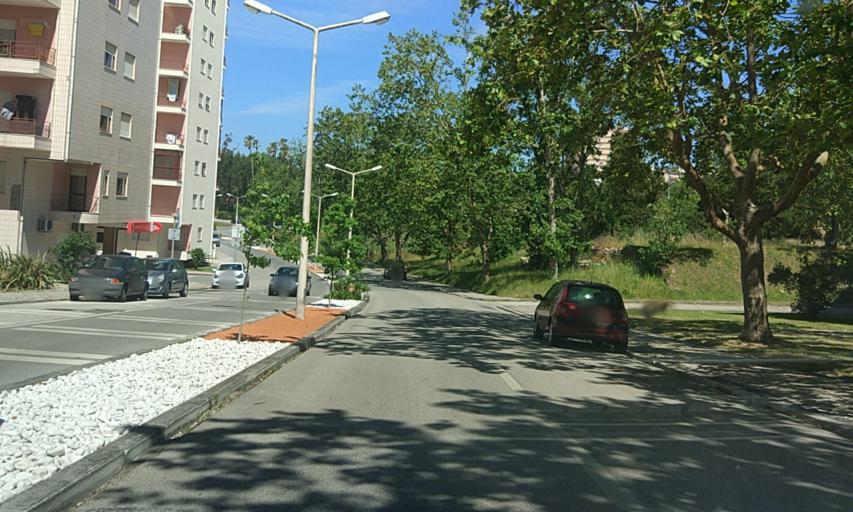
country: PT
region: Coimbra
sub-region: Figueira da Foz
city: Figueira da Foz
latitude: 40.1547
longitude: -8.8589
